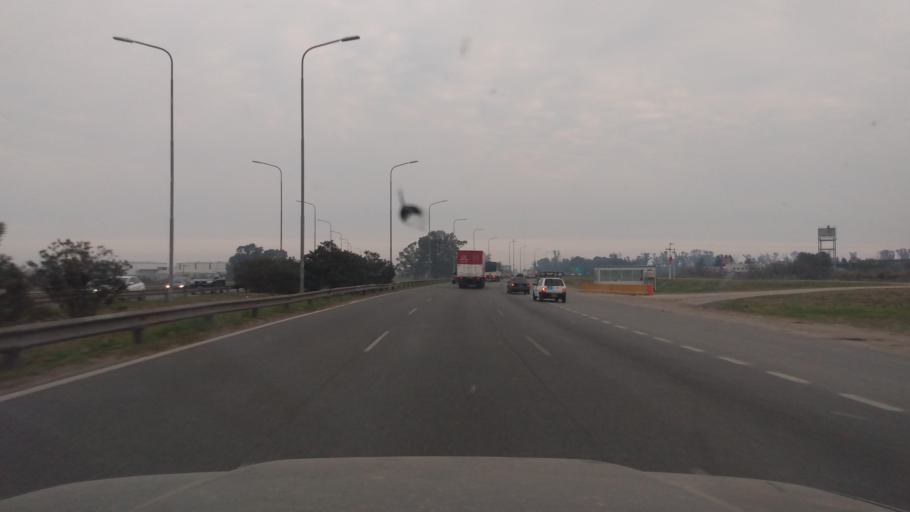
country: AR
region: Buenos Aires
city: Hurlingham
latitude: -34.5198
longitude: -58.5911
